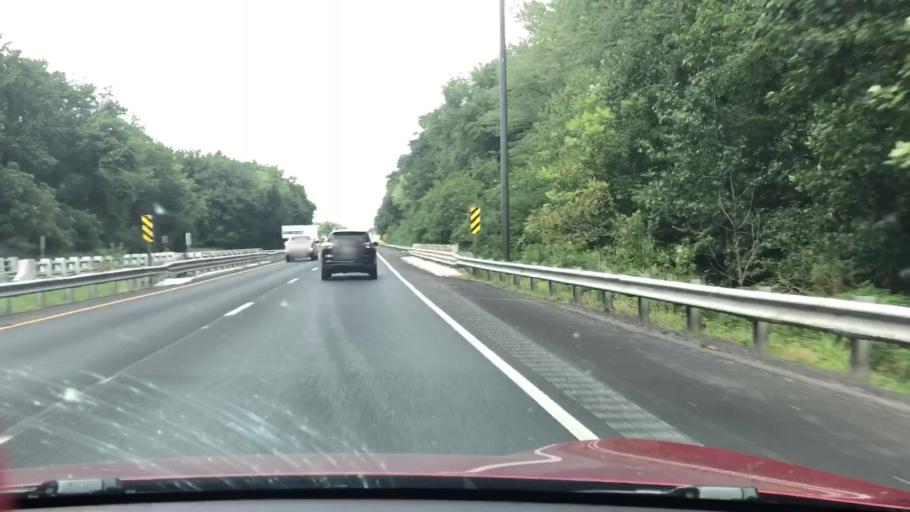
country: US
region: Maryland
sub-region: Worcester County
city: Pocomoke City
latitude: 38.0087
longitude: -75.5446
